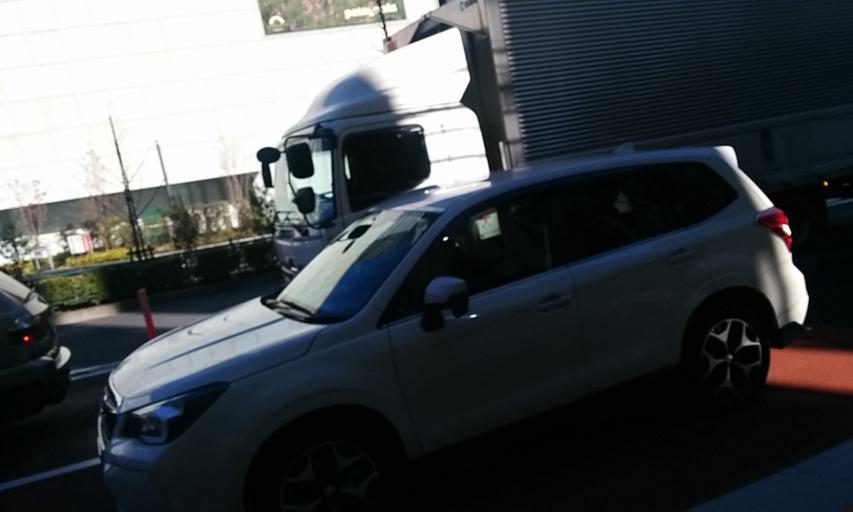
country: JP
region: Tokyo
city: Tokyo
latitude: 35.6186
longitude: 139.7300
